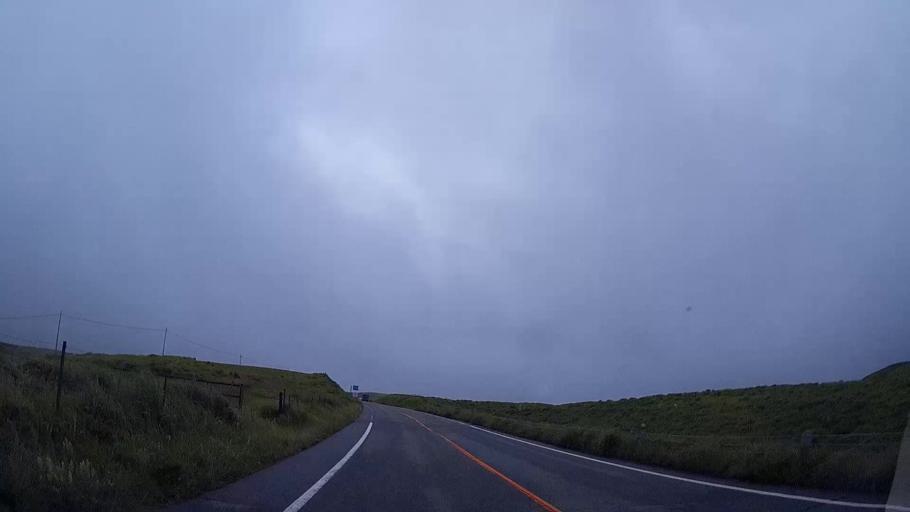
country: JP
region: Kumamoto
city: Aso
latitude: 33.0048
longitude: 131.0699
